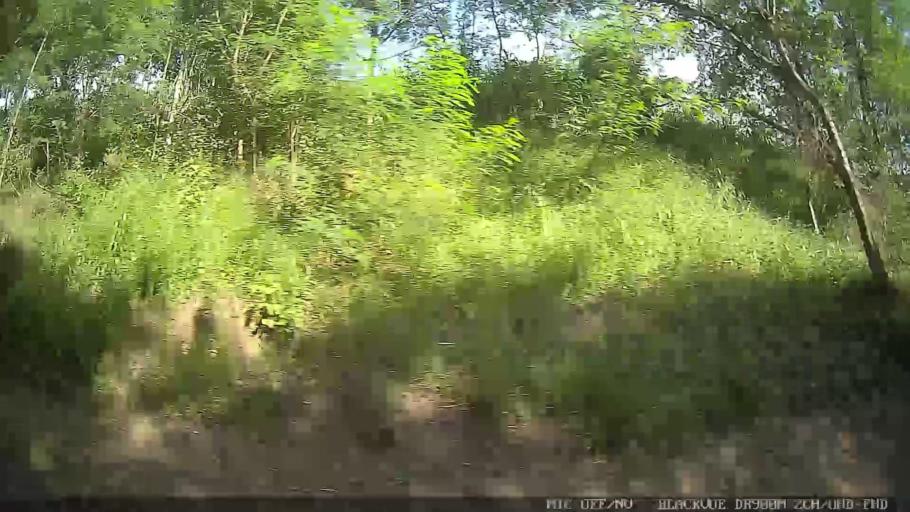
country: BR
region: Sao Paulo
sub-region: Tiete
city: Tiete
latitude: -23.1029
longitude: -47.6924
